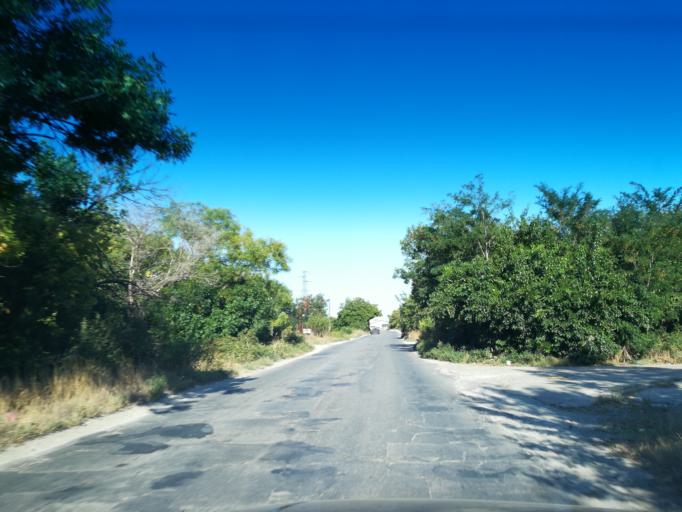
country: BG
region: Plovdiv
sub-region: Obshtina Plovdiv
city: Plovdiv
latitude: 42.1659
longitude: 24.8063
